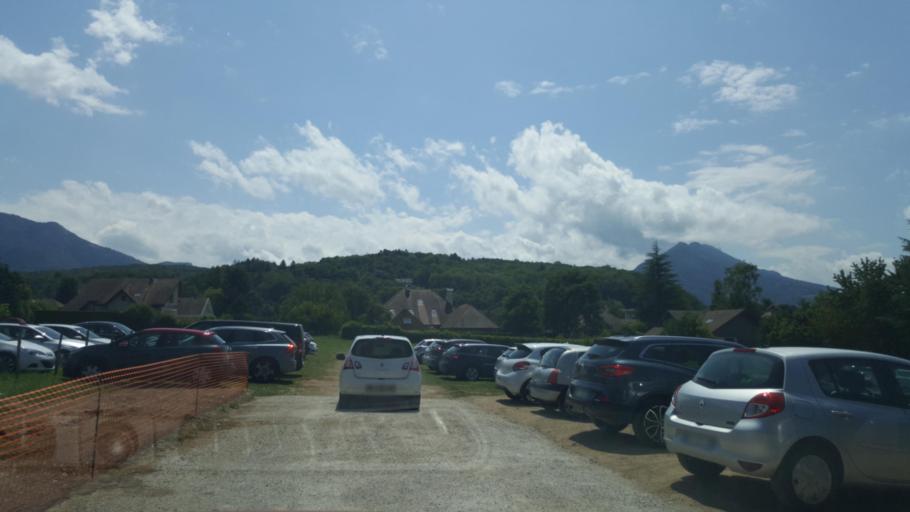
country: FR
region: Rhone-Alpes
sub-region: Departement de la Haute-Savoie
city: Menthon-Saint-Bernard
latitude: 45.8603
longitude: 6.1890
